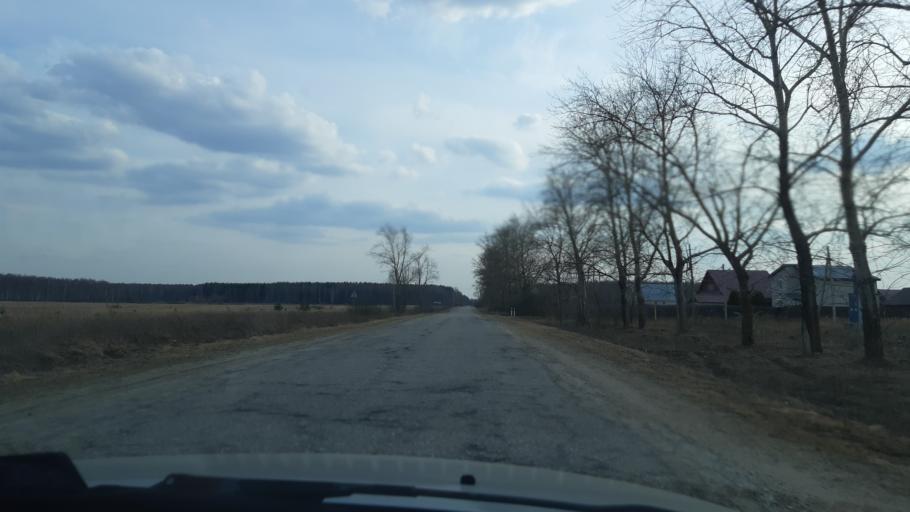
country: RU
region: Vladimir
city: Nikologory
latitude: 56.1263
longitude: 41.9886
